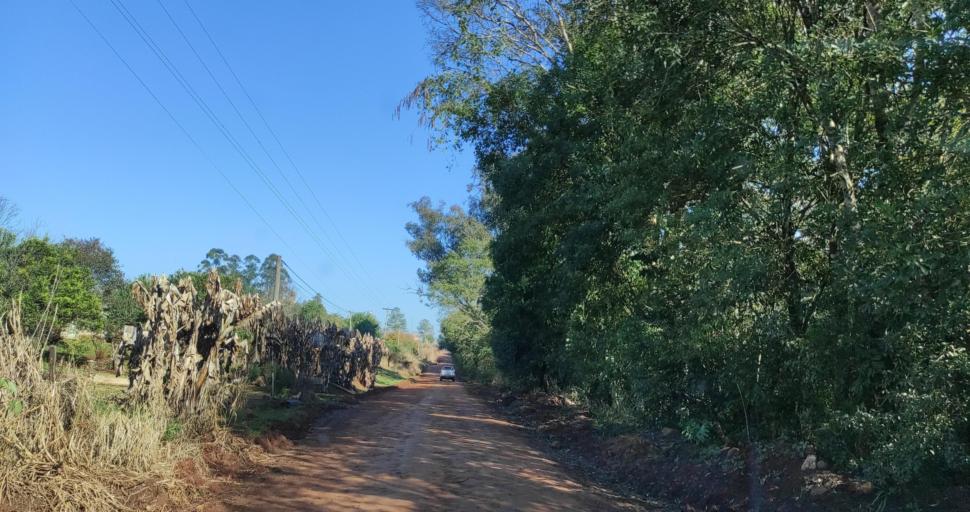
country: AR
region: Misiones
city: Capiovi
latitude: -26.8645
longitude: -55.0404
